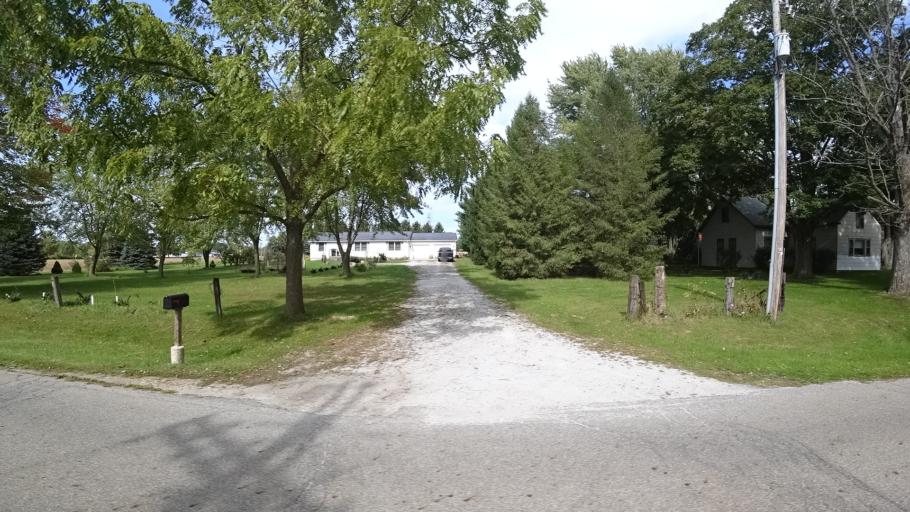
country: US
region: Indiana
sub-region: LaPorte County
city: Trail Creek
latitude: 41.7092
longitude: -86.8386
